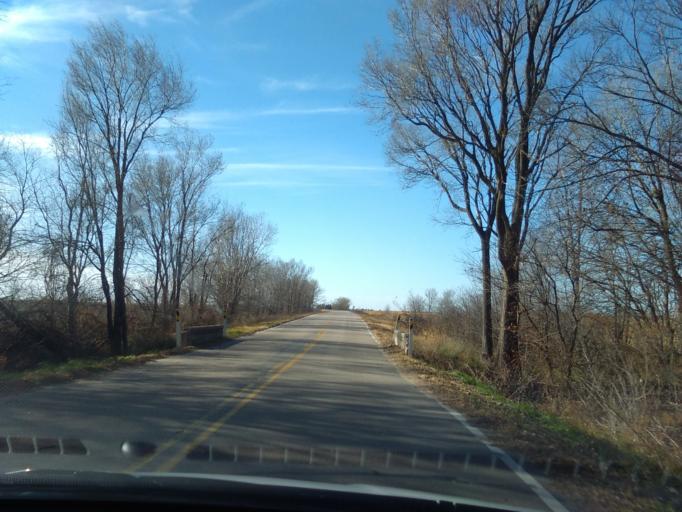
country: US
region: Nebraska
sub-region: Adams County
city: Hastings
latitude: 40.5100
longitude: -98.2459
